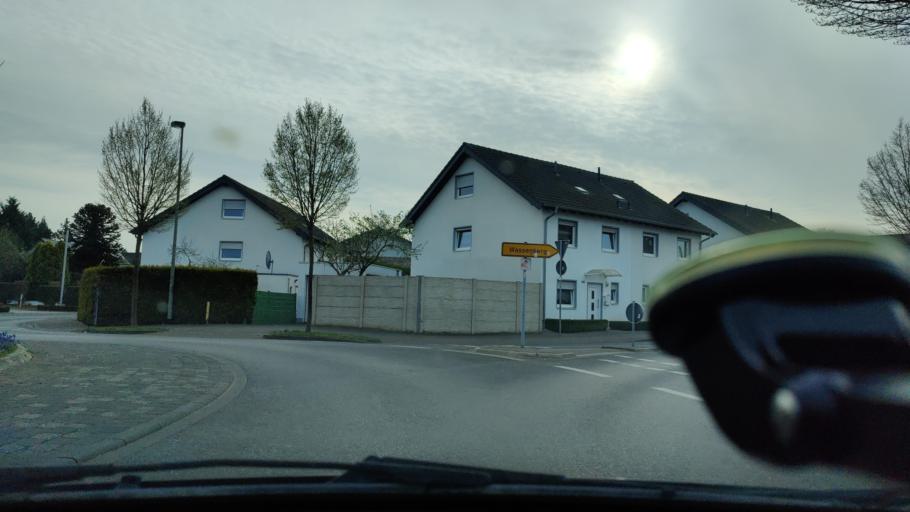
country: DE
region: North Rhine-Westphalia
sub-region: Regierungsbezirk Koln
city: Wassenberg
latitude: 51.1012
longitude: 6.1822
